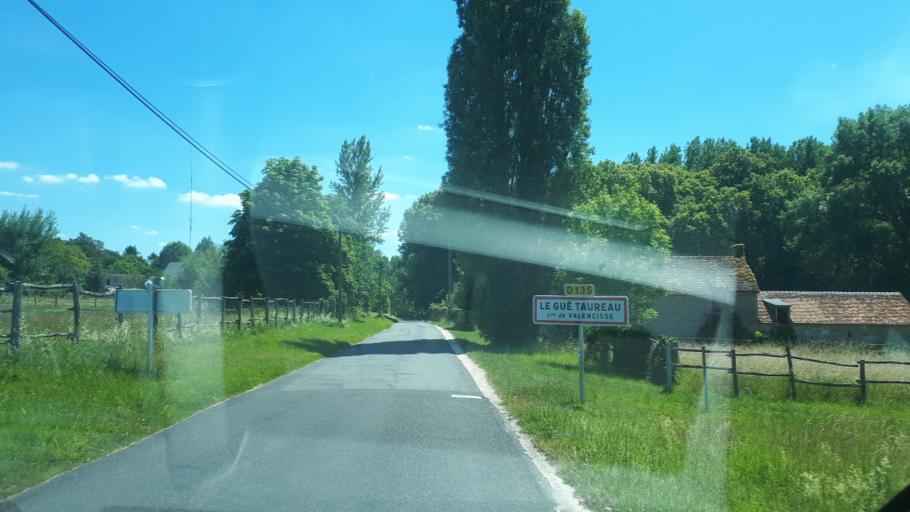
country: FR
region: Centre
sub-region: Departement du Loir-et-Cher
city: Saint-Sulpice-de-Pommeray
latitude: 47.5878
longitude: 1.2074
